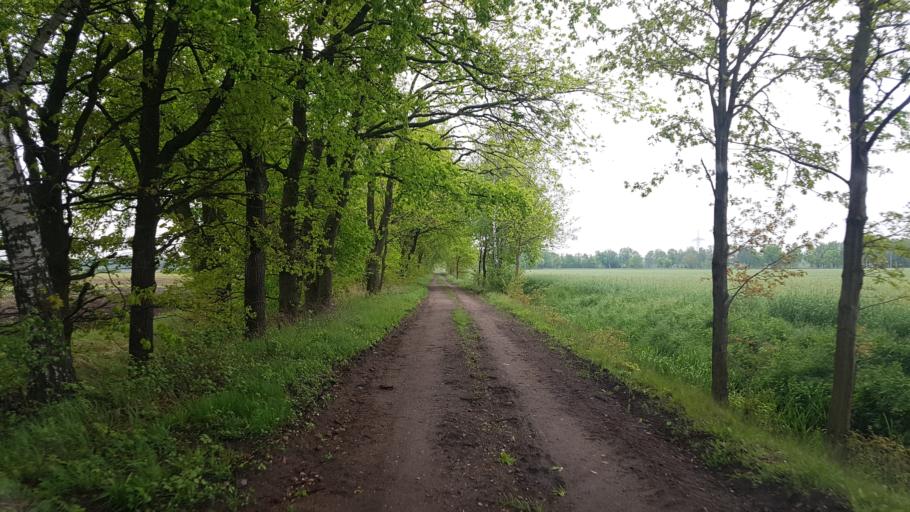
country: DE
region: Brandenburg
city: Elsterwerda
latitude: 51.4372
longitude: 13.5444
